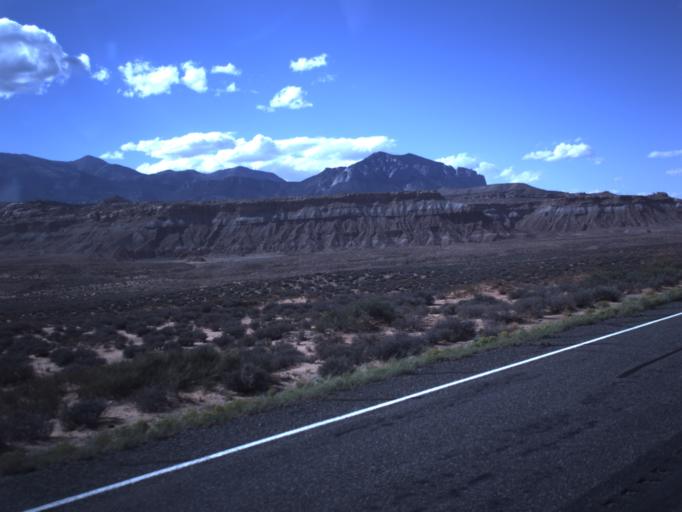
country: US
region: Utah
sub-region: Wayne County
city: Loa
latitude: 38.0829
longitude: -110.6136
